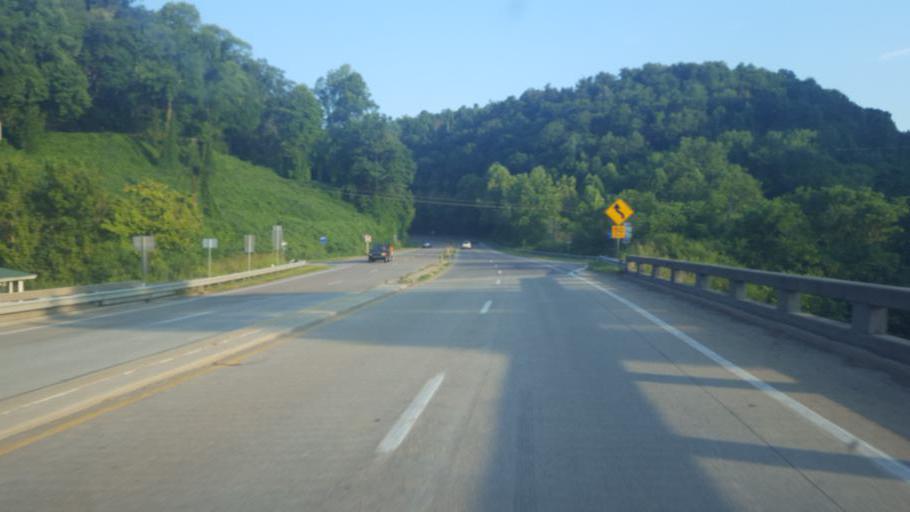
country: US
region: Tennessee
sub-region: Hawkins County
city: Church Hill
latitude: 36.6483
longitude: -82.7495
